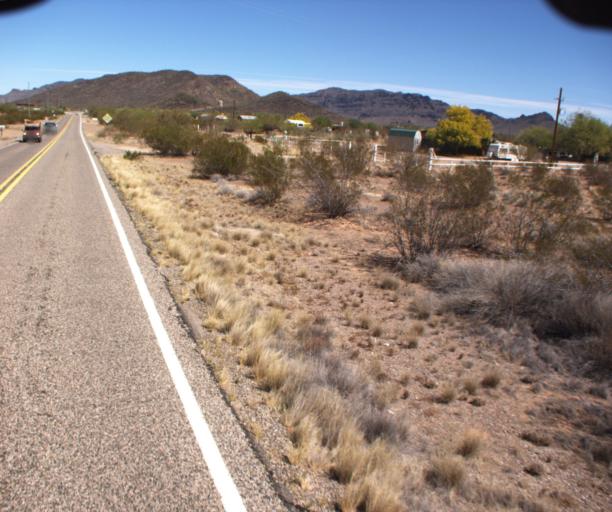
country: US
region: Arizona
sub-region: Pima County
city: Ajo
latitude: 32.2584
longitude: -112.7425
